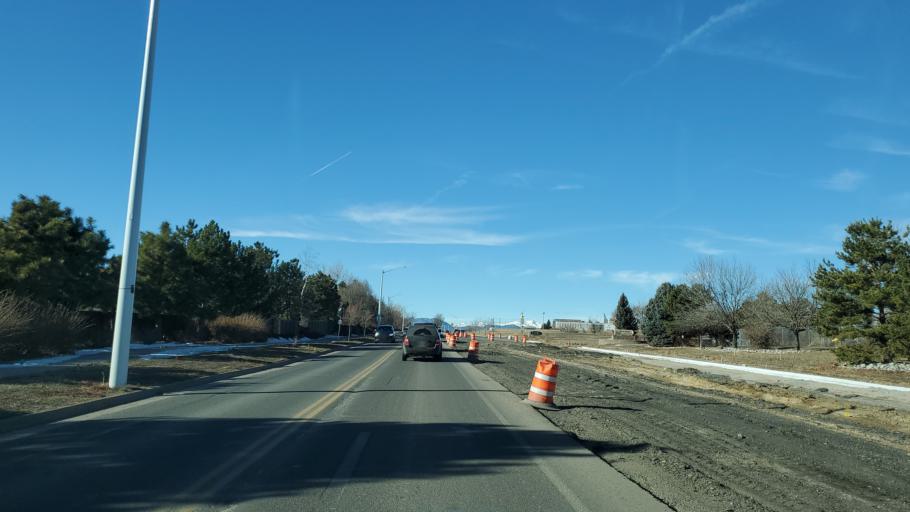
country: US
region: Colorado
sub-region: Broomfield County
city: Broomfield
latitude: 39.9576
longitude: -105.0420
